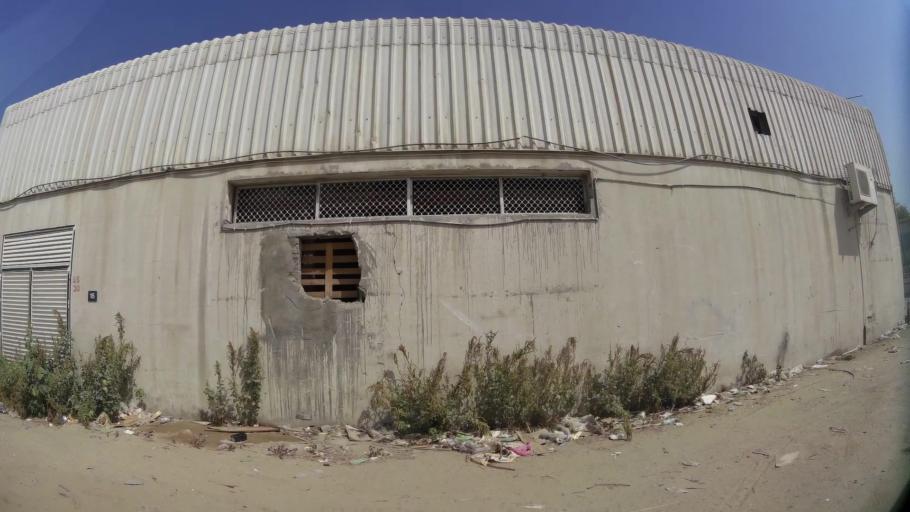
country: AE
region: Ash Shariqah
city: Sharjah
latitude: 25.3079
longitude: 55.3881
